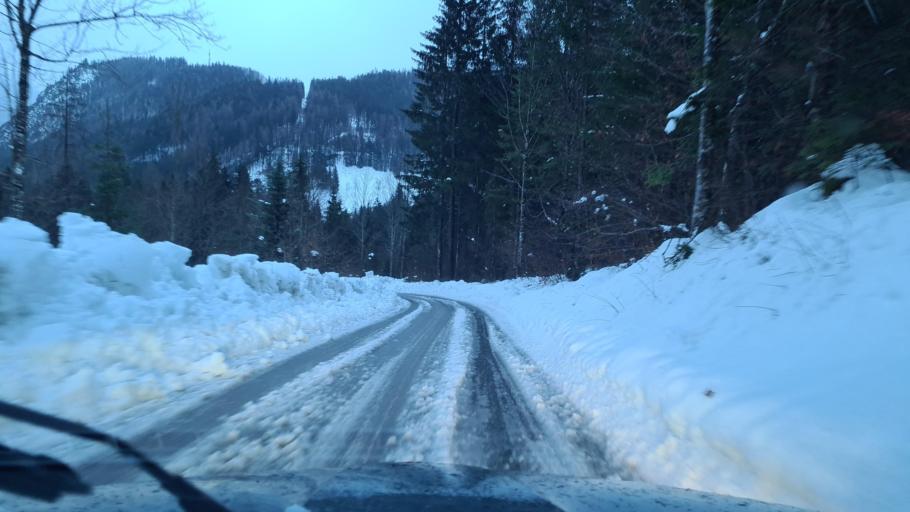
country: AT
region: Salzburg
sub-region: Politischer Bezirk Sankt Johann im Pongau
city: Werfen
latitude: 47.4906
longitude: 13.1605
